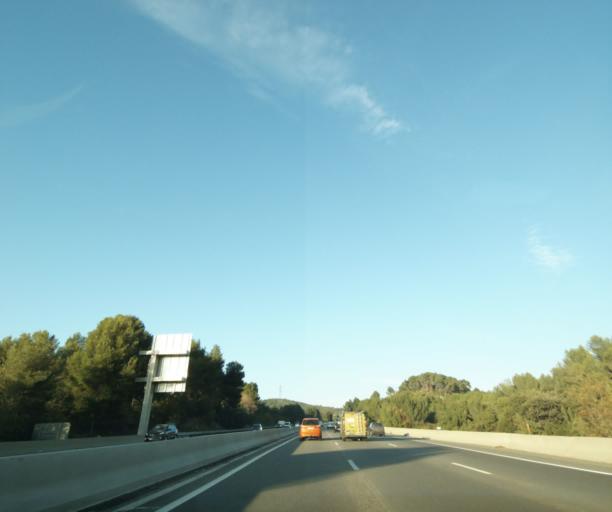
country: FR
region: Provence-Alpes-Cote d'Azur
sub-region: Departement des Bouches-du-Rhone
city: Roquevaire
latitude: 43.3387
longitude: 5.6085
